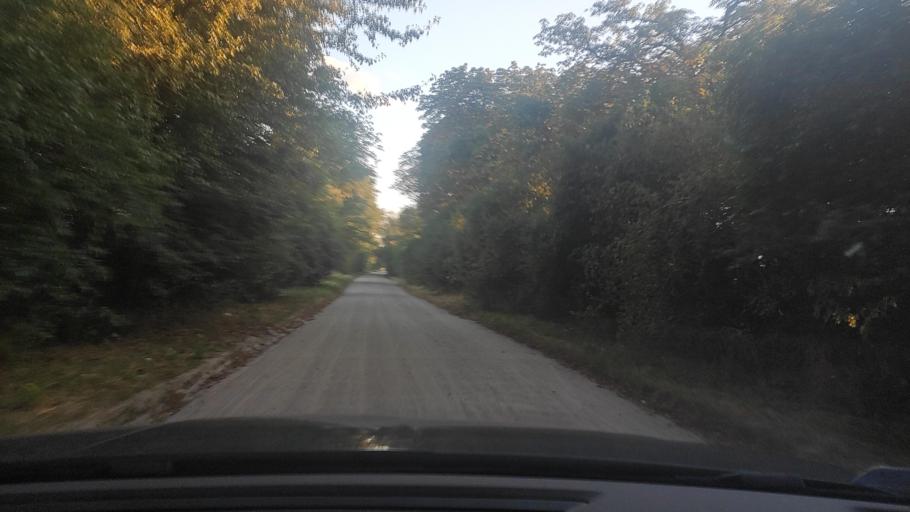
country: PL
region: Greater Poland Voivodeship
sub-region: Powiat poznanski
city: Swarzedz
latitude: 52.4382
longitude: 17.1217
